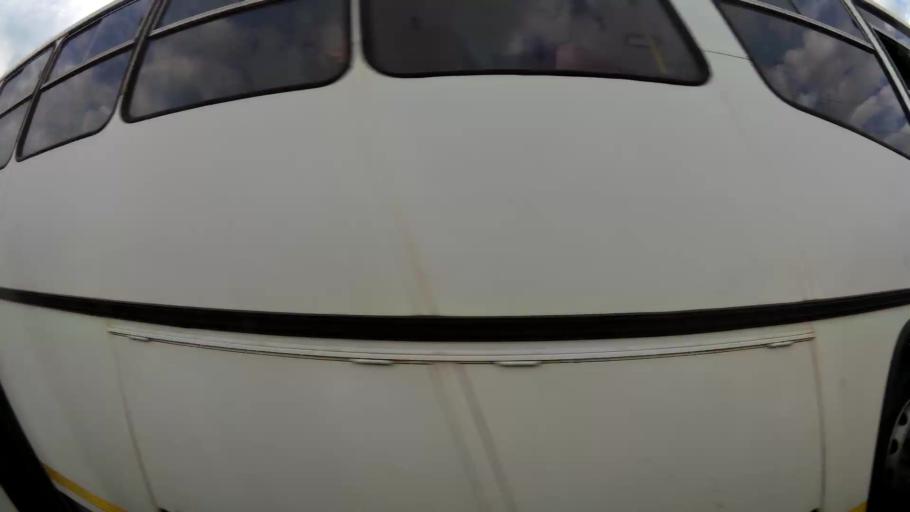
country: ZA
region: Limpopo
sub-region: Waterberg District Municipality
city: Modimolle
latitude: -24.5202
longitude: 28.7170
